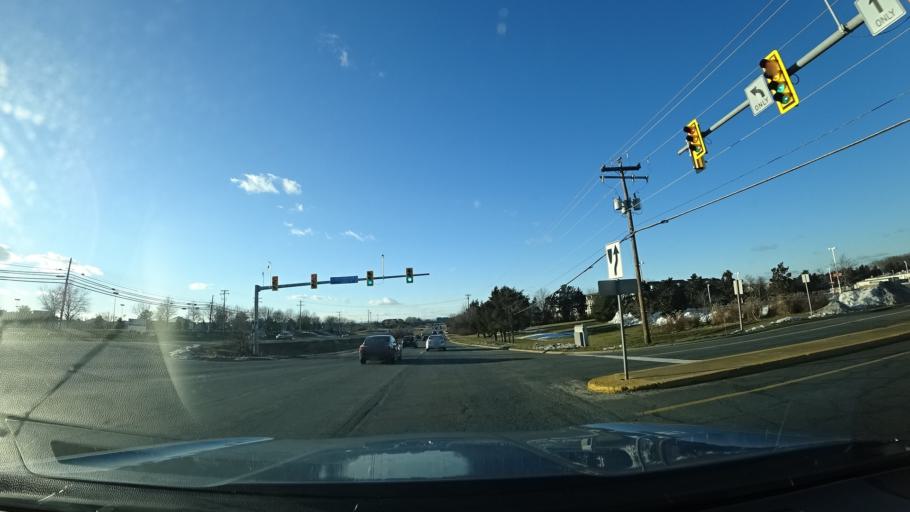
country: US
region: Virginia
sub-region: Loudoun County
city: Sugarland Run
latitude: 39.0267
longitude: -77.3943
